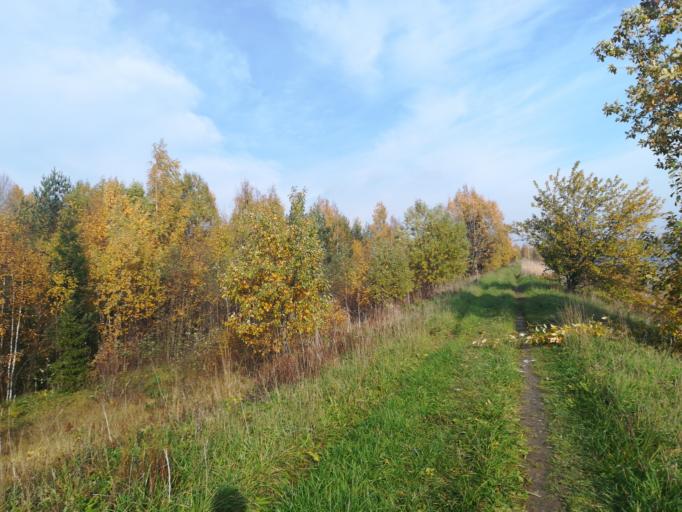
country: RU
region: Leningrad
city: Sista-Palkino
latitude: 59.5898
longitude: 28.8247
